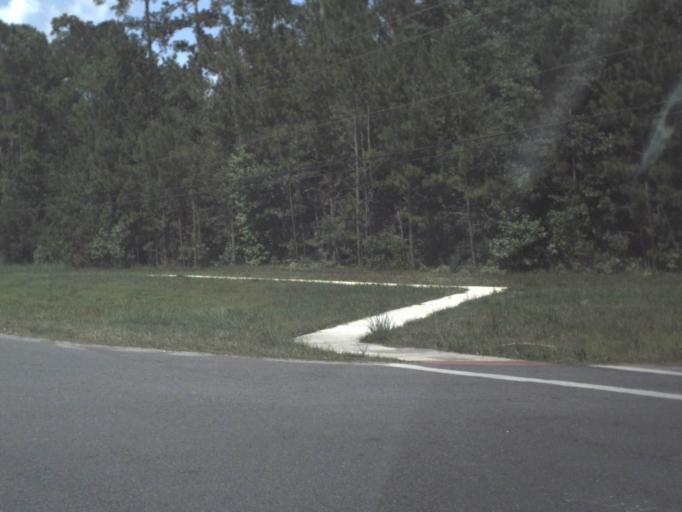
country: US
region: Florida
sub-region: Clay County
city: Green Cove Springs
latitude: 30.0574
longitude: -81.7077
